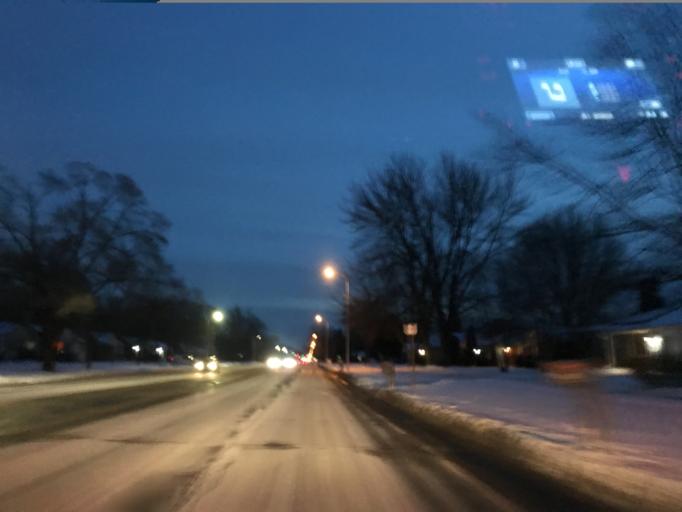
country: US
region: Michigan
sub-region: Wayne County
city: Redford
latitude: 42.3960
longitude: -83.3149
